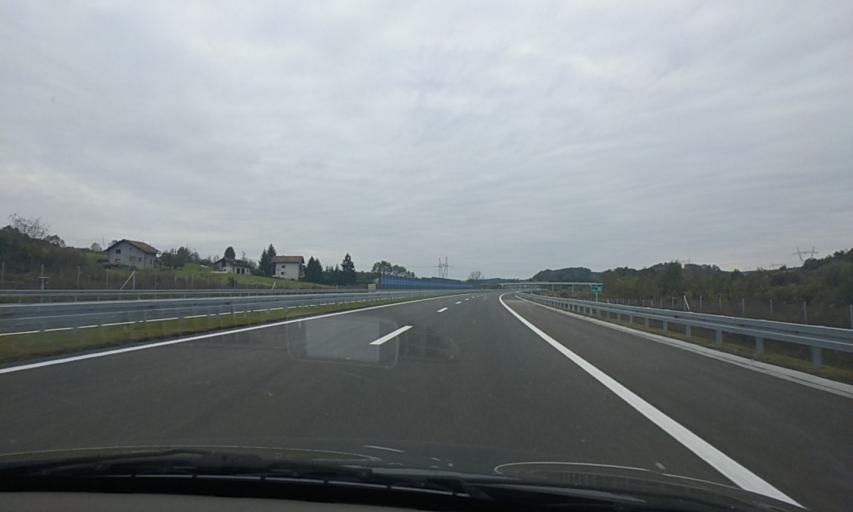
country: BA
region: Republika Srpska
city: Prnjavor
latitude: 44.8906
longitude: 17.5785
